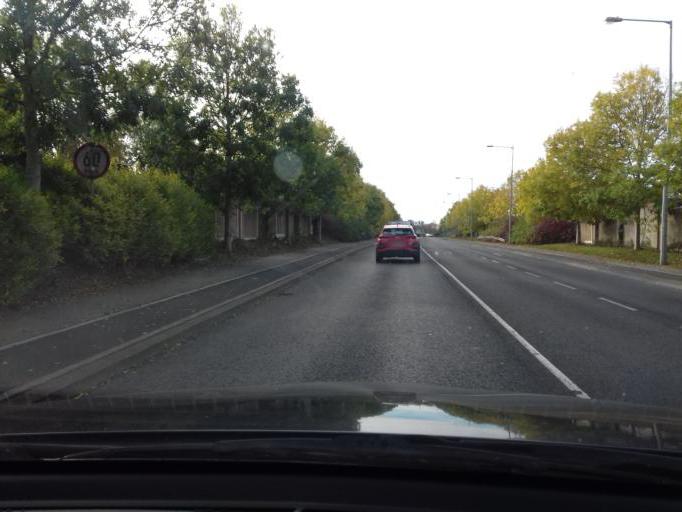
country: IE
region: Leinster
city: Hartstown
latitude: 53.3902
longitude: -6.4134
